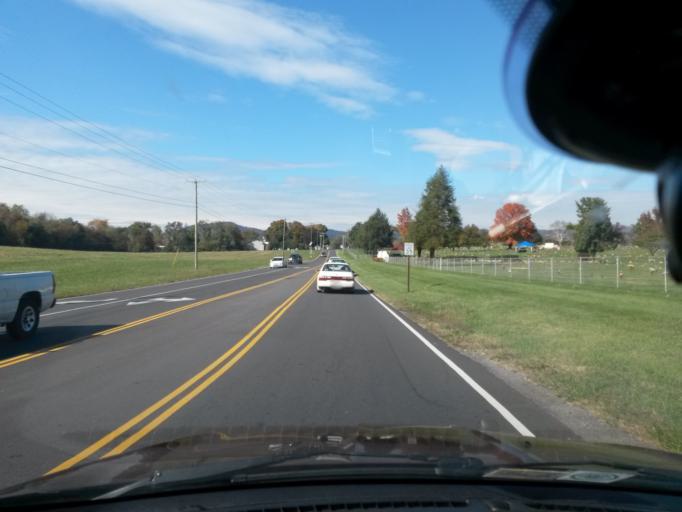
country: US
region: Virginia
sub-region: Roanoke County
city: Hollins
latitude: 37.3246
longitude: -79.9636
